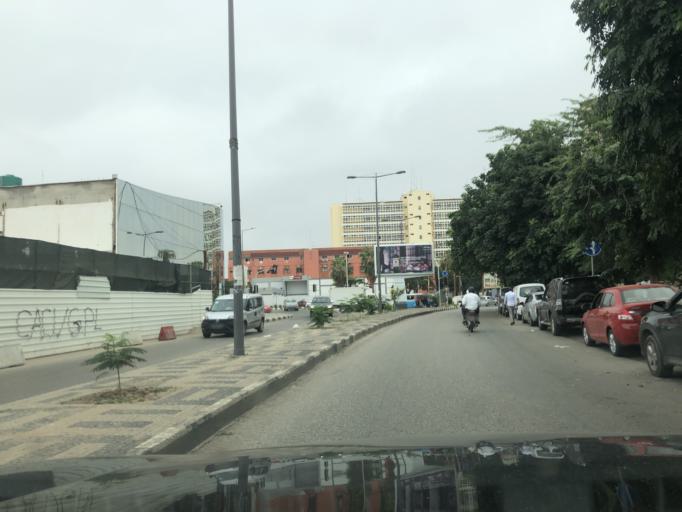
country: AO
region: Luanda
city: Luanda
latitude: -8.8270
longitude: 13.2389
